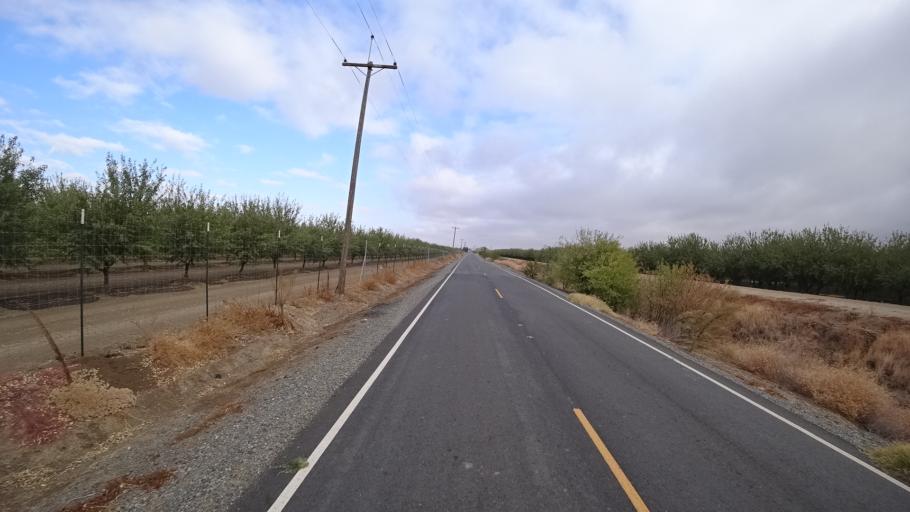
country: US
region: California
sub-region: Yolo County
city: Esparto
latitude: 38.7625
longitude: -122.0442
